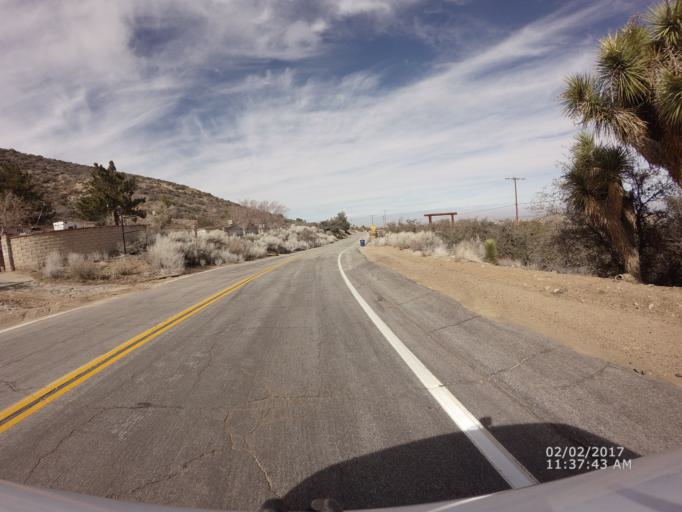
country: US
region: California
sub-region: Los Angeles County
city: Littlerock
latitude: 34.4268
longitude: -117.9173
